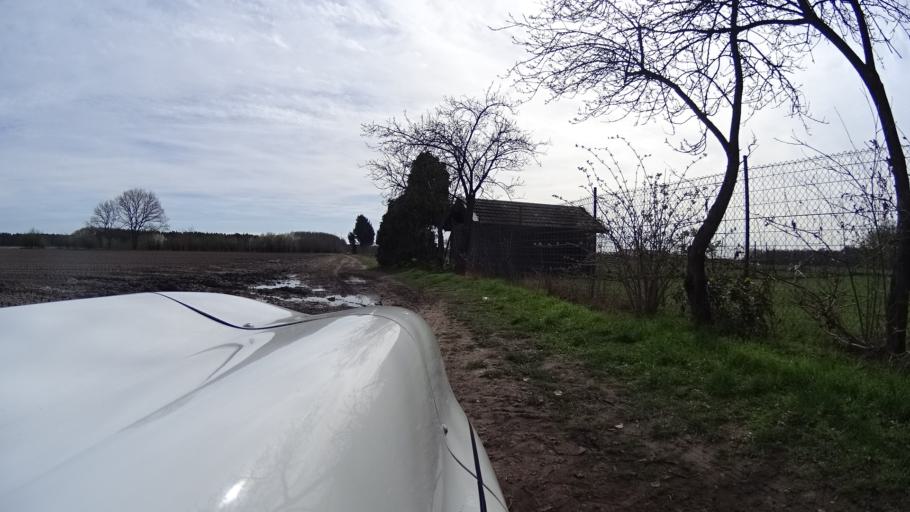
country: NL
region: Limburg
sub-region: Gemeente Venlo
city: Arcen
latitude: 51.5249
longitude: 6.2024
